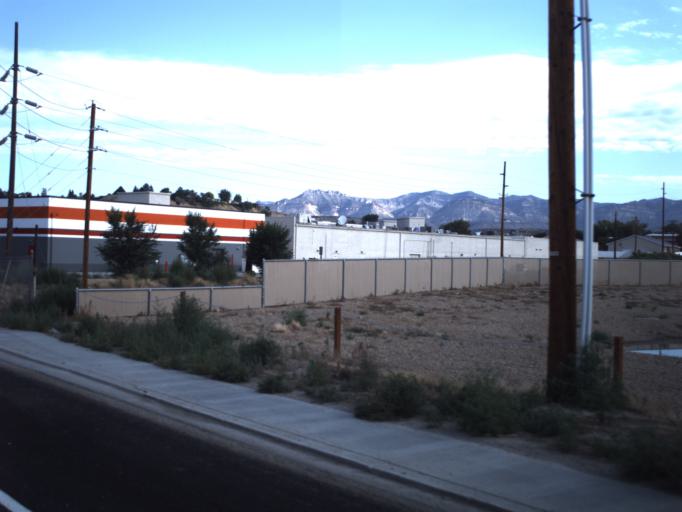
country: US
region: Utah
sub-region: Carbon County
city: Price
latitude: 39.5981
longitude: -110.7927
